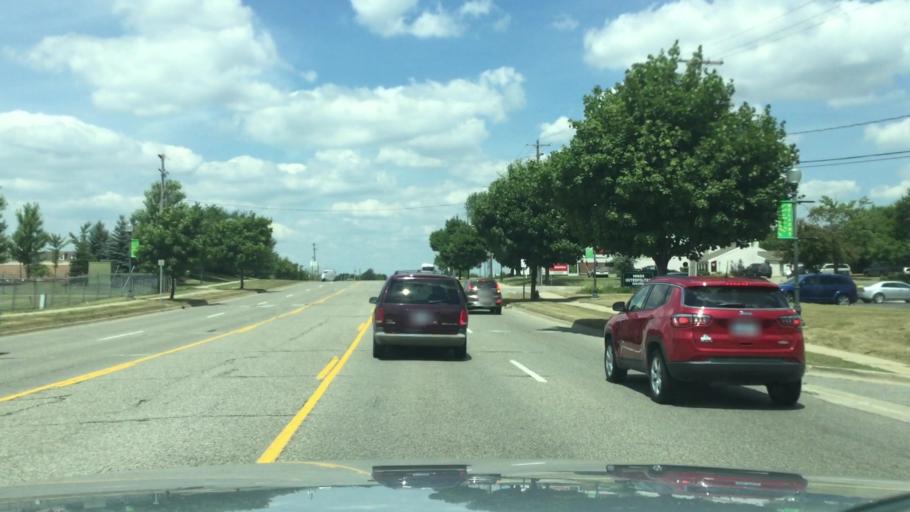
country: US
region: Michigan
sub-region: Genesee County
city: Grand Blanc
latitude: 42.9366
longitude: -83.6409
